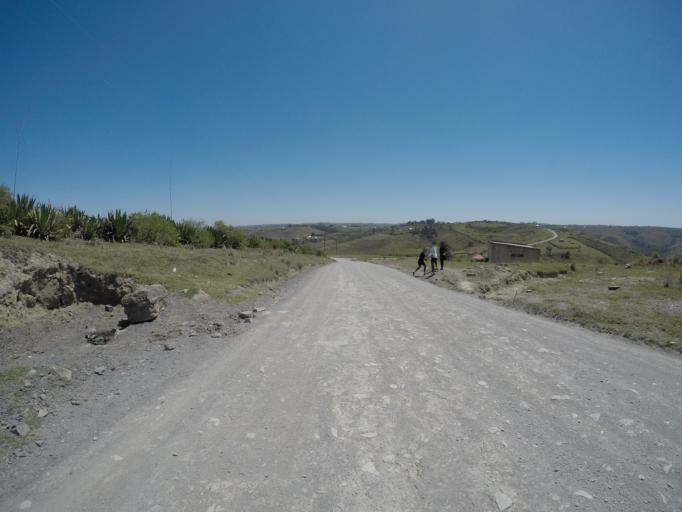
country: ZA
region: Eastern Cape
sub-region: OR Tambo District Municipality
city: Libode
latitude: -31.9822
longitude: 29.0358
